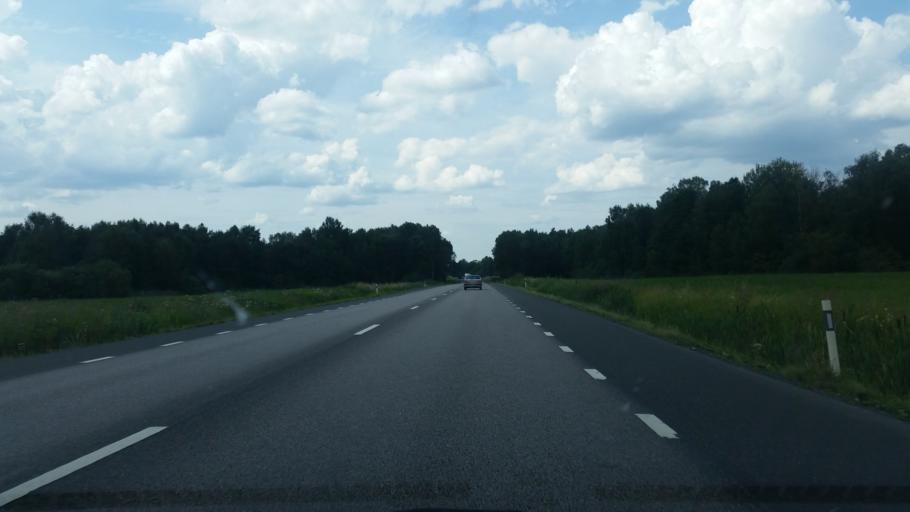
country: SE
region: Vaestra Goetaland
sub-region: Skara Kommun
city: Axvall
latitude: 58.3911
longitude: 13.6455
